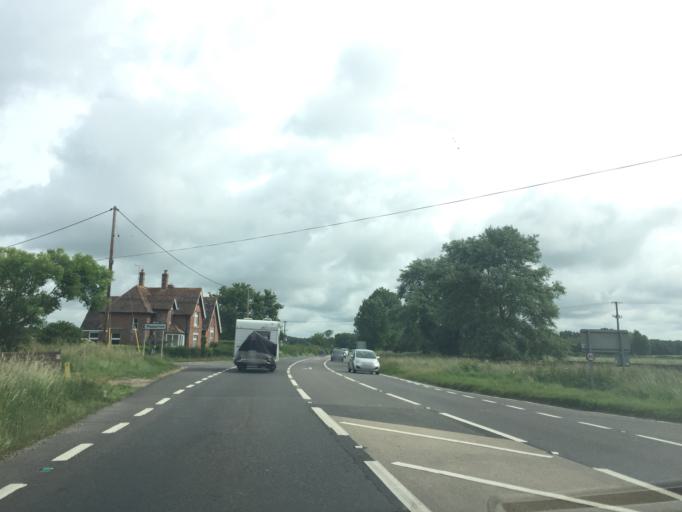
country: GB
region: England
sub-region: Dorset
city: Lytchett Matravers
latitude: 50.7817
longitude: -2.1323
